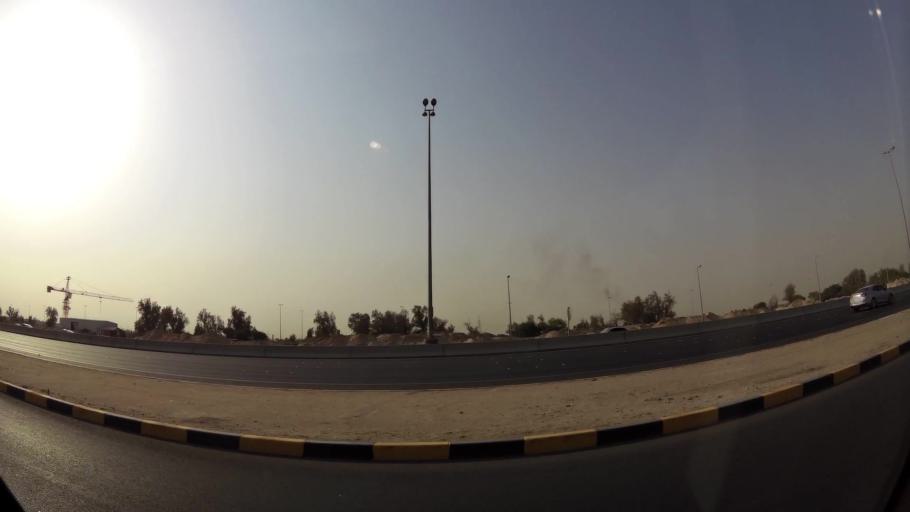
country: KW
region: Al Asimah
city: Ar Rabiyah
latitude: 29.3111
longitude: 47.8237
